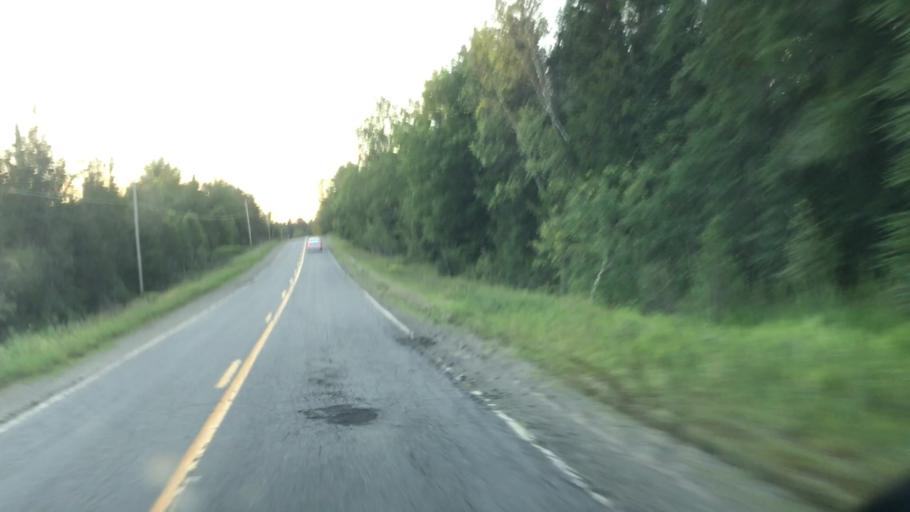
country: US
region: Maine
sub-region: Penobscot County
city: Medway
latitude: 45.6030
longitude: -68.2516
